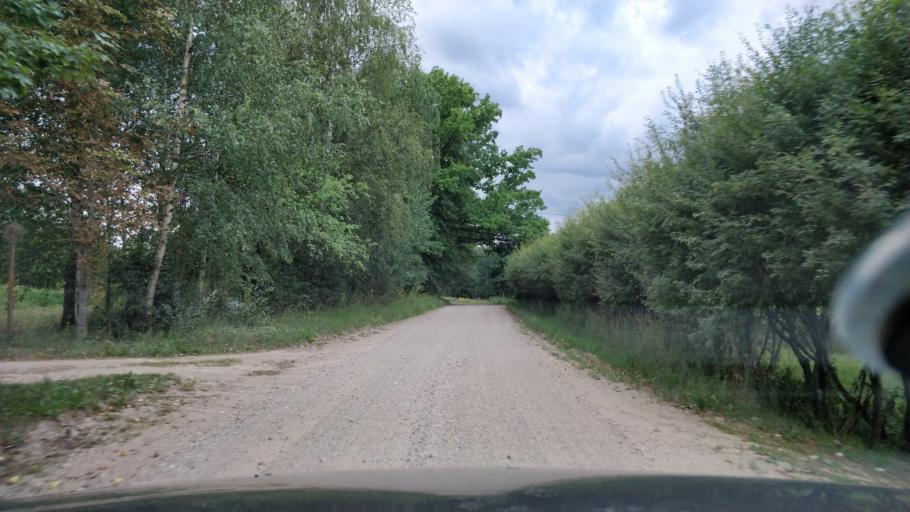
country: LV
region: Ogre
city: Ogre
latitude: 56.8025
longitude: 24.6803
